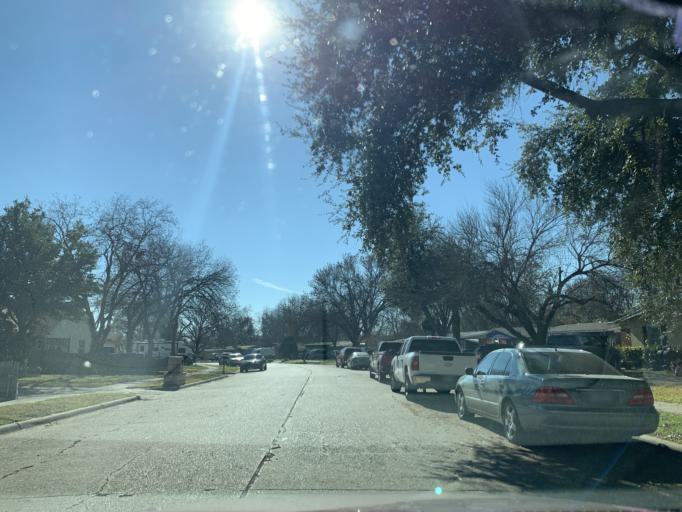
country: US
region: Texas
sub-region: Tarrant County
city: Arlington
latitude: 32.7337
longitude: -97.0693
